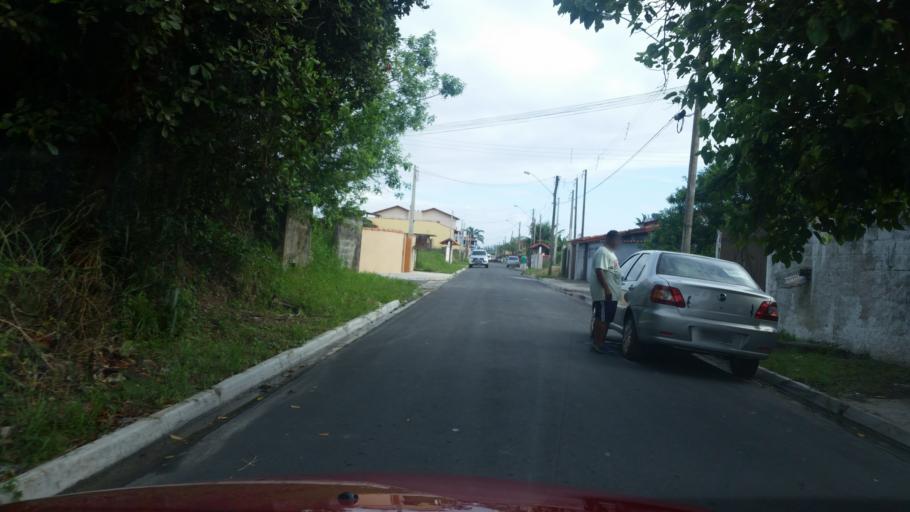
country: BR
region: Sao Paulo
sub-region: Iguape
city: Iguape
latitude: -24.7386
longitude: -47.5517
